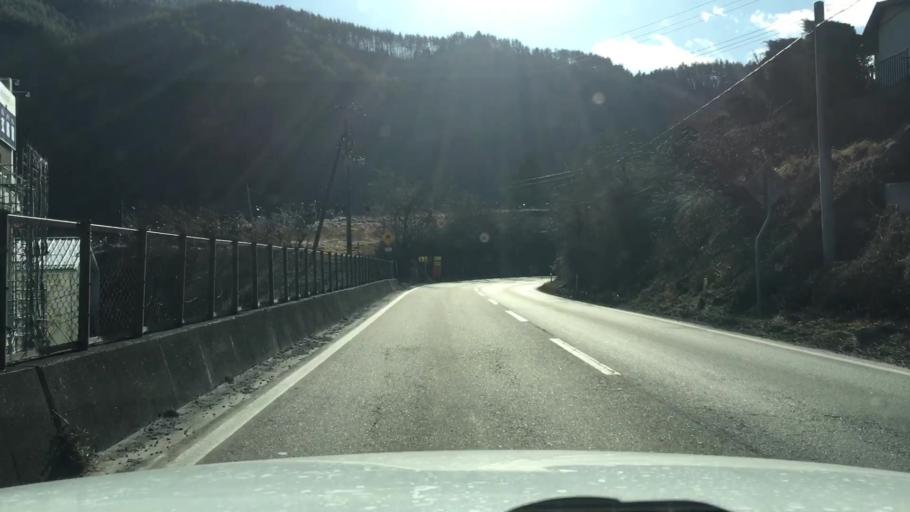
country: JP
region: Iwate
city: Miyako
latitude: 39.6166
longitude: 141.7992
